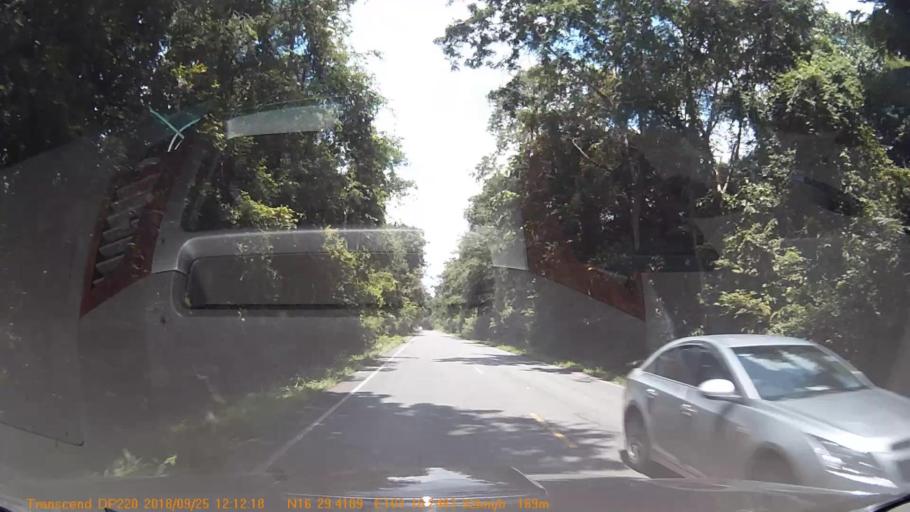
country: TH
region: Kalasin
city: Huai Mek
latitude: 16.4904
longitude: 103.2708
